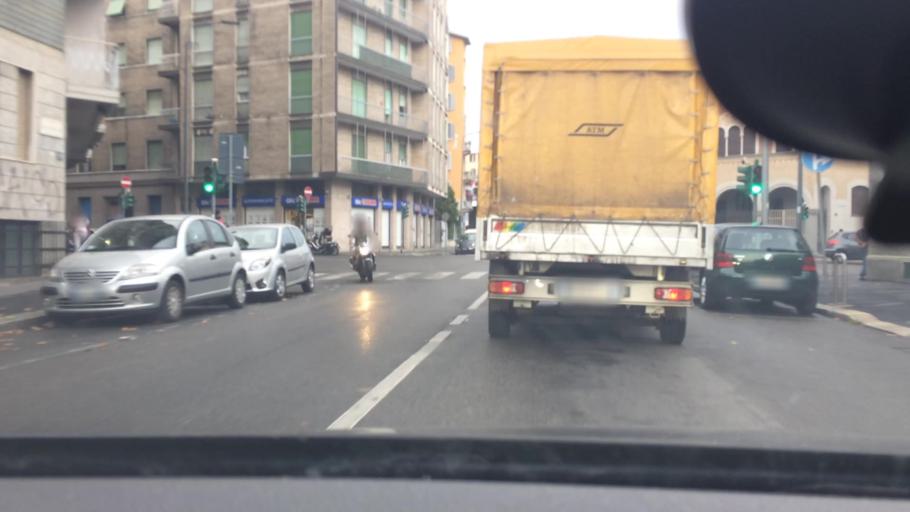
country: IT
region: Lombardy
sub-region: Citta metropolitana di Milano
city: Sesto San Giovanni
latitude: 45.4959
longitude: 9.2209
